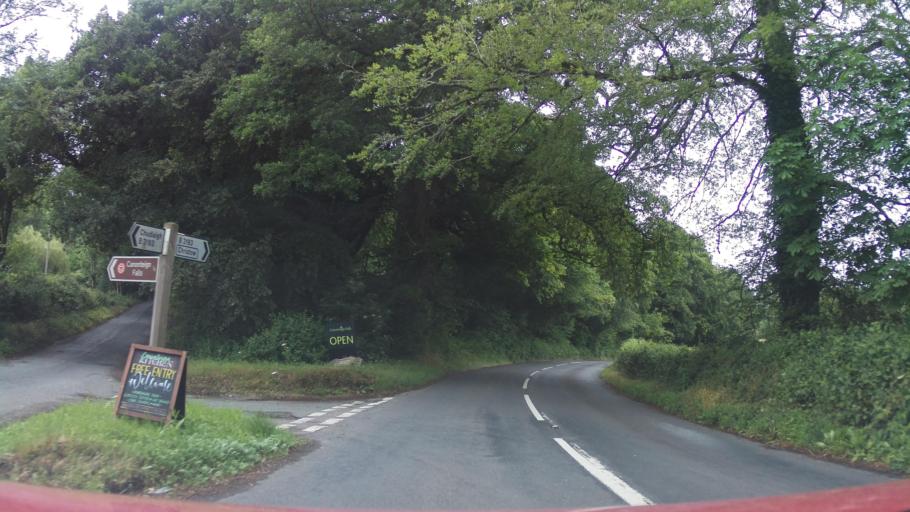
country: GB
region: England
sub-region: Devon
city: Chudleigh
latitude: 50.6284
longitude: -3.6413
